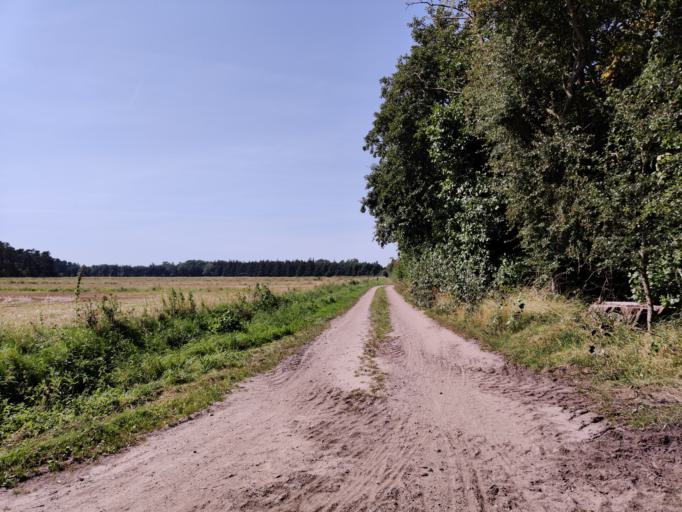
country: DK
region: Zealand
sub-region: Guldborgsund Kommune
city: Nykobing Falster
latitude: 54.6126
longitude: 11.9573
